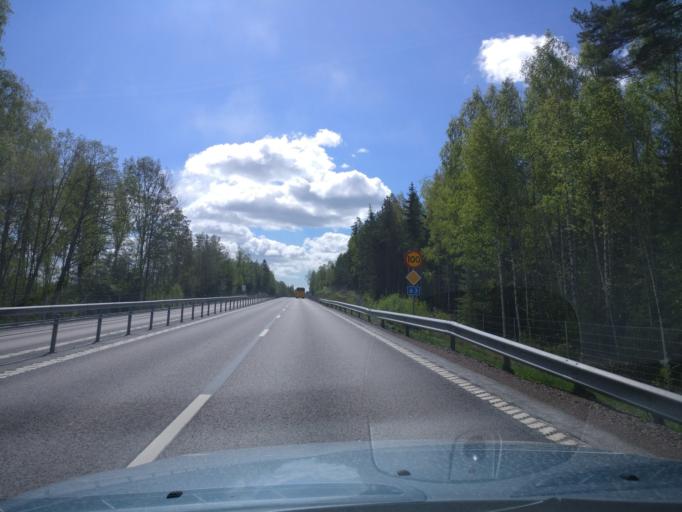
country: SE
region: Vaermland
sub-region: Karlstads Kommun
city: Karlstad
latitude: 59.4441
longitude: 13.5443
